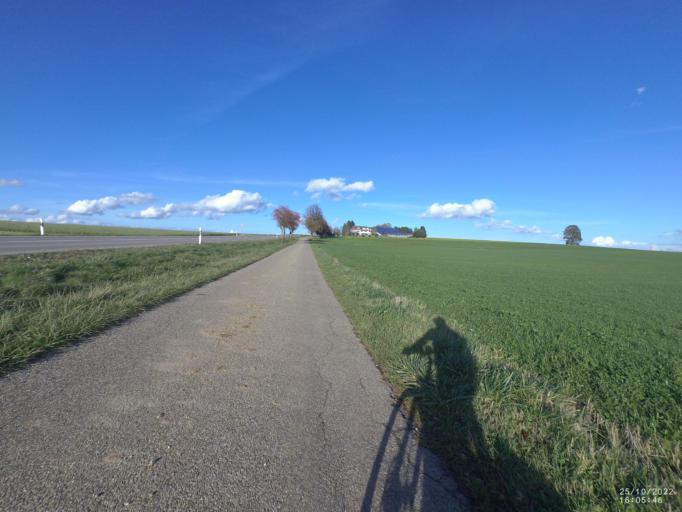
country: DE
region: Baden-Wuerttemberg
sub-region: Regierungsbezirk Stuttgart
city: Bohmenkirch
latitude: 48.6693
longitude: 9.9158
